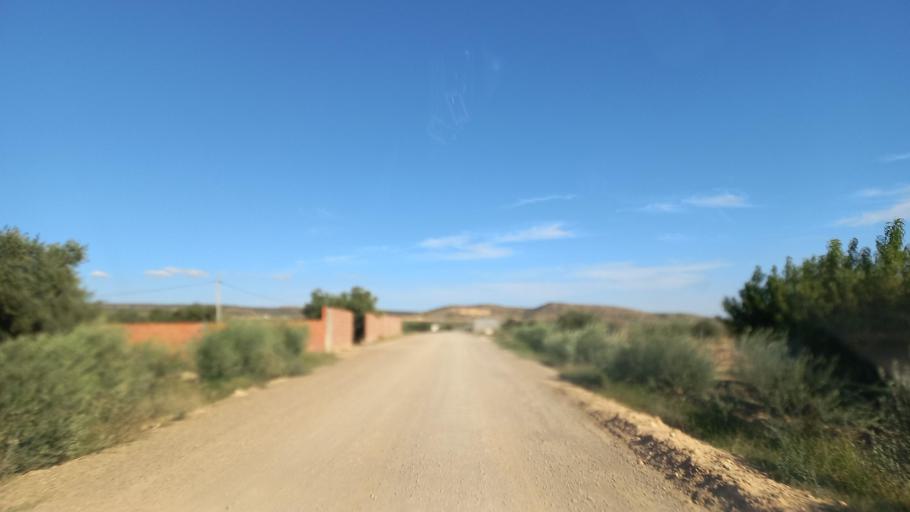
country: TN
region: Al Qasrayn
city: Sbiba
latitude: 35.2967
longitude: 9.0995
